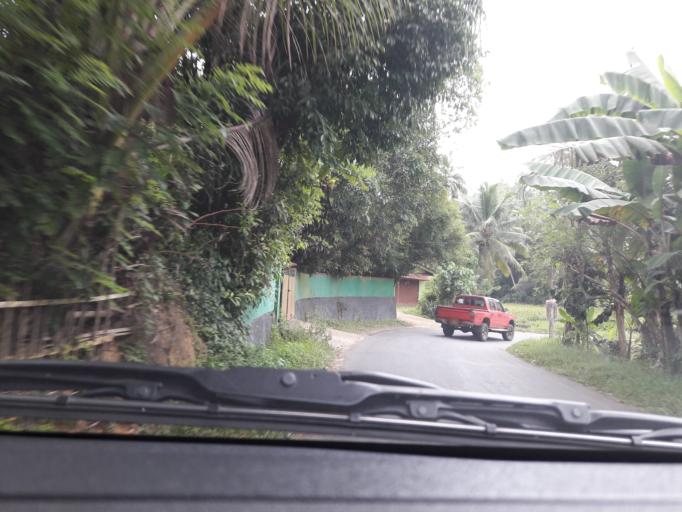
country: LK
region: Southern
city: Unawatuna
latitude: 6.0600
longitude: 80.2505
